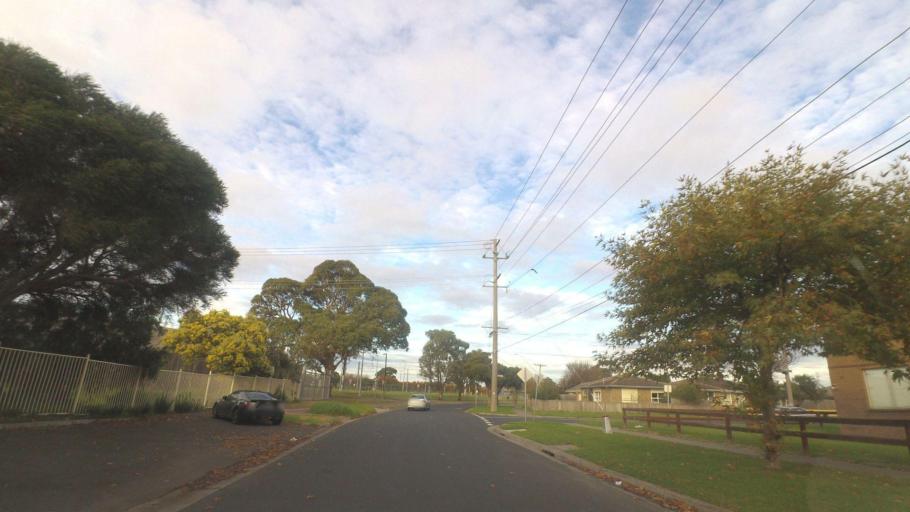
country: AU
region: Victoria
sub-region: Kingston
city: Clayton South
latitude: -37.9358
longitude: 145.1343
